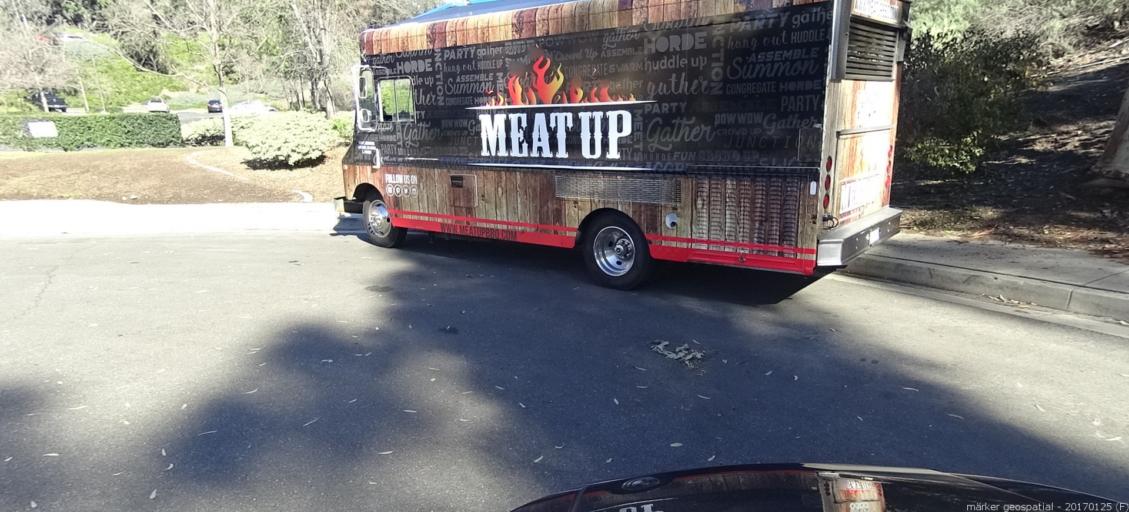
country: US
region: California
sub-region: Orange County
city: Lake Forest
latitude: 33.6610
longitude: -117.6913
